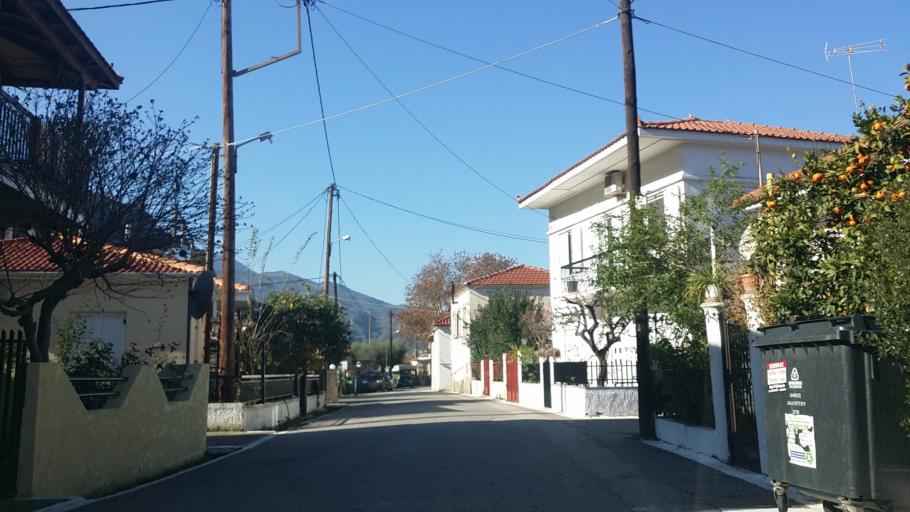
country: GR
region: West Greece
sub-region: Nomos Achaias
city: Temeni
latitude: 38.1877
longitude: 22.1835
